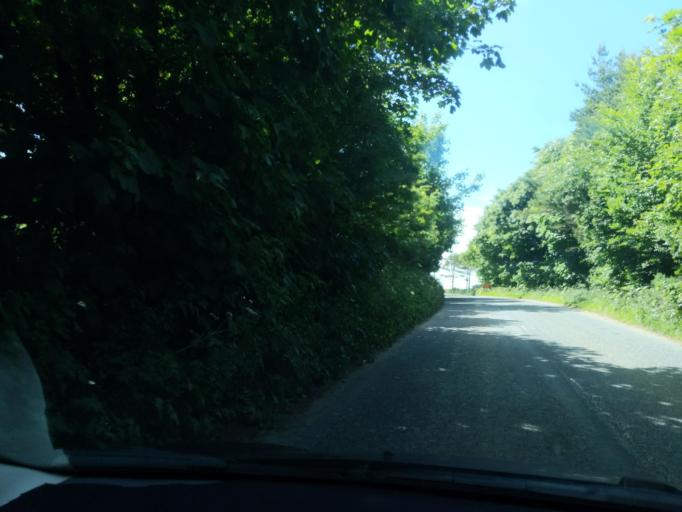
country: GB
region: England
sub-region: Cornwall
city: Perranporth
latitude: 50.2981
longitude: -5.1428
